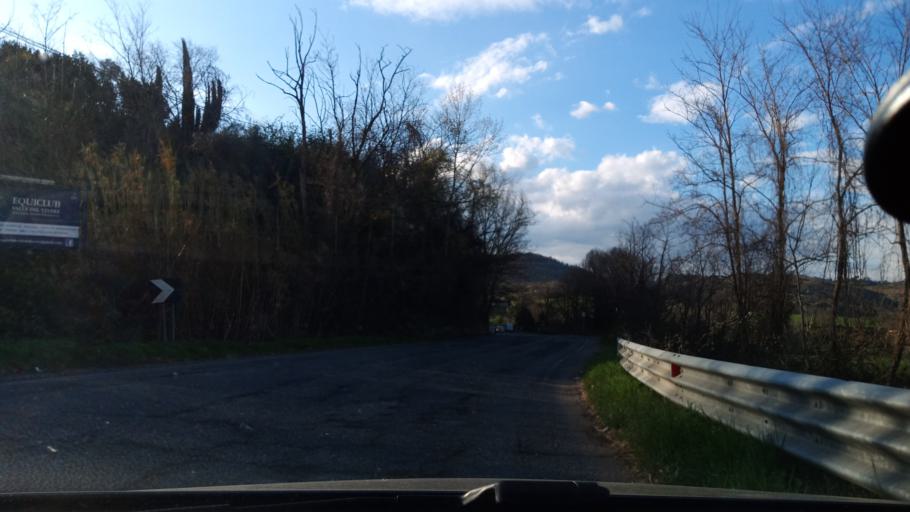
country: IT
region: Latium
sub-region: Citta metropolitana di Roma Capitale
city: Fiano Romano
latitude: 42.1789
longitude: 12.6079
